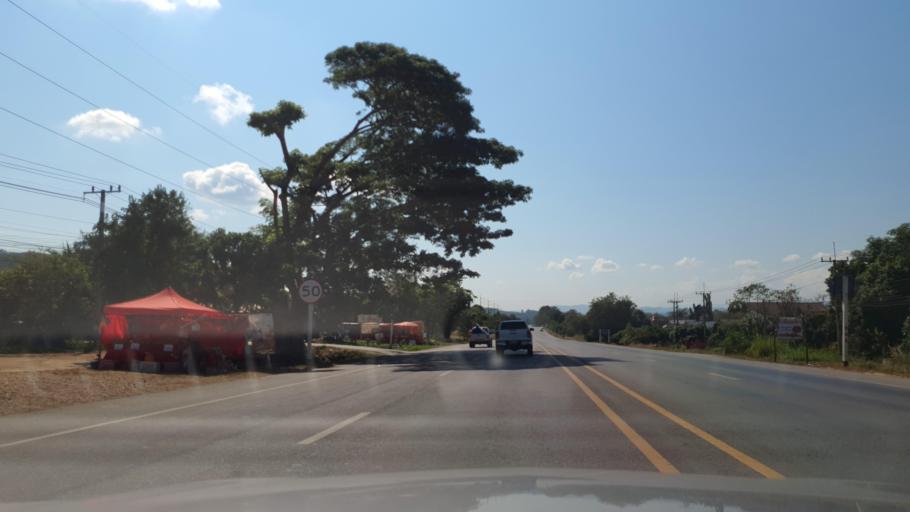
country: TH
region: Nan
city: Tha Wang Pha
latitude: 19.0391
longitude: 100.8030
